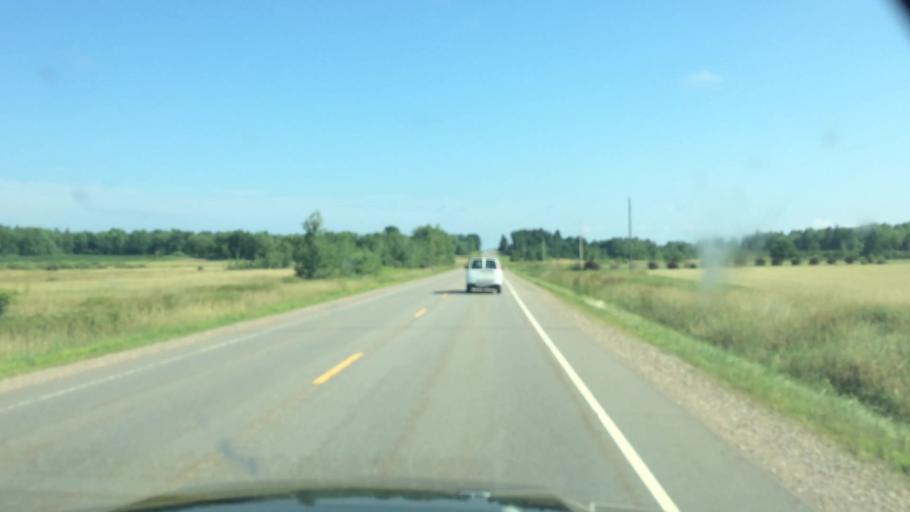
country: US
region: Wisconsin
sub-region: Lincoln County
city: Merrill
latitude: 45.1570
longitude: -89.4666
